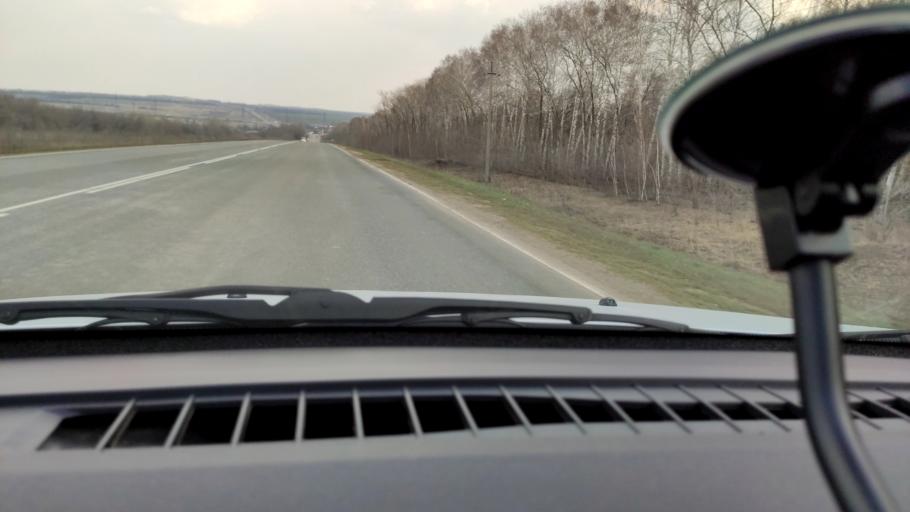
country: RU
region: Samara
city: Dubovyy Umet
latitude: 53.0733
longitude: 50.3581
